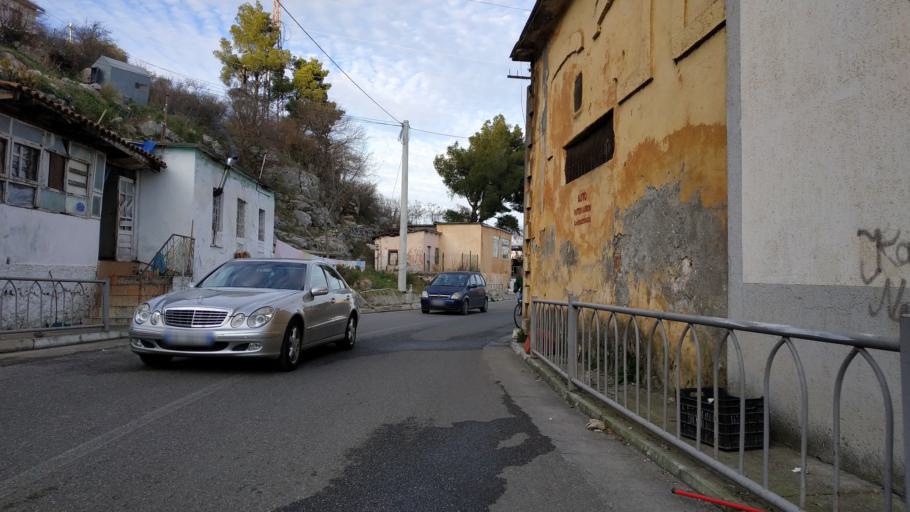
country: AL
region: Shkoder
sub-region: Rrethi i Shkodres
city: Shkoder
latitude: 42.0518
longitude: 19.4902
